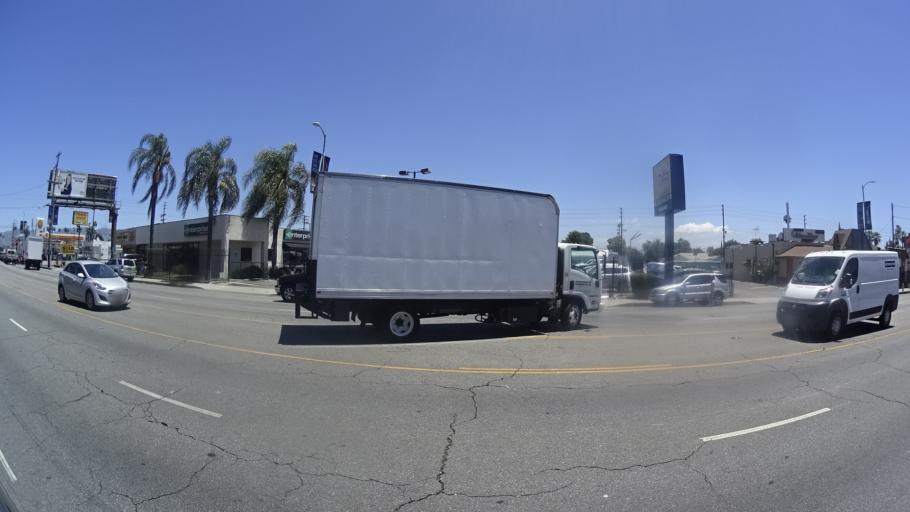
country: US
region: California
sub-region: Los Angeles County
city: Van Nuys
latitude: 34.2203
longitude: -118.4677
